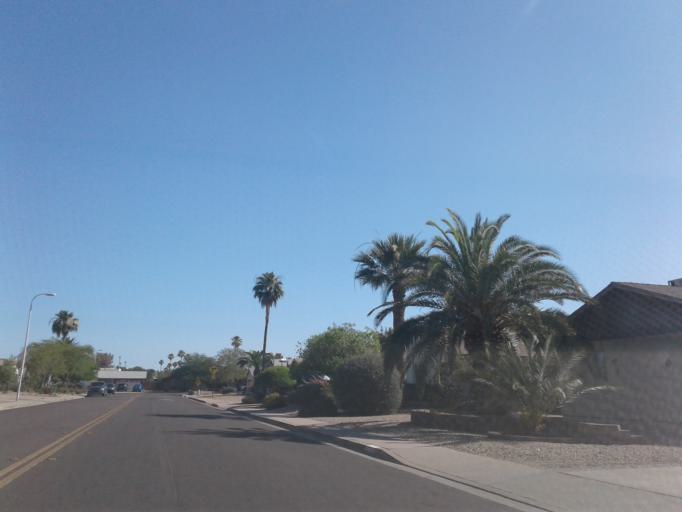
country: US
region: Arizona
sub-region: Maricopa County
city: Scottsdale
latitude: 33.4933
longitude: -111.8951
